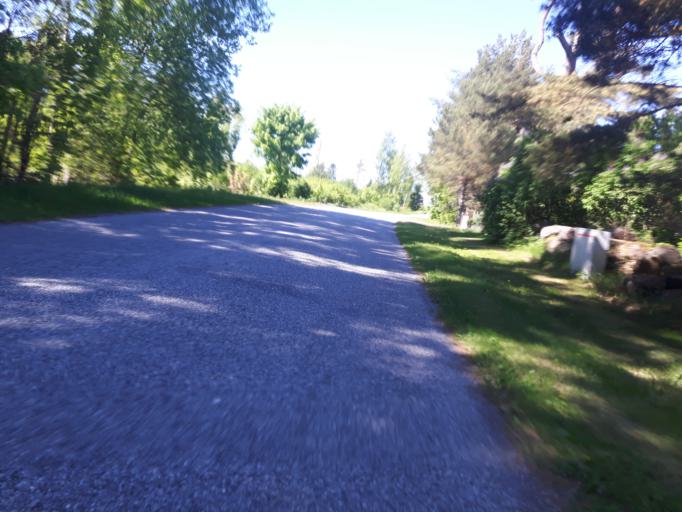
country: EE
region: Laeaene-Virumaa
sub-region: Haljala vald
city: Haljala
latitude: 59.5632
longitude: 26.3103
